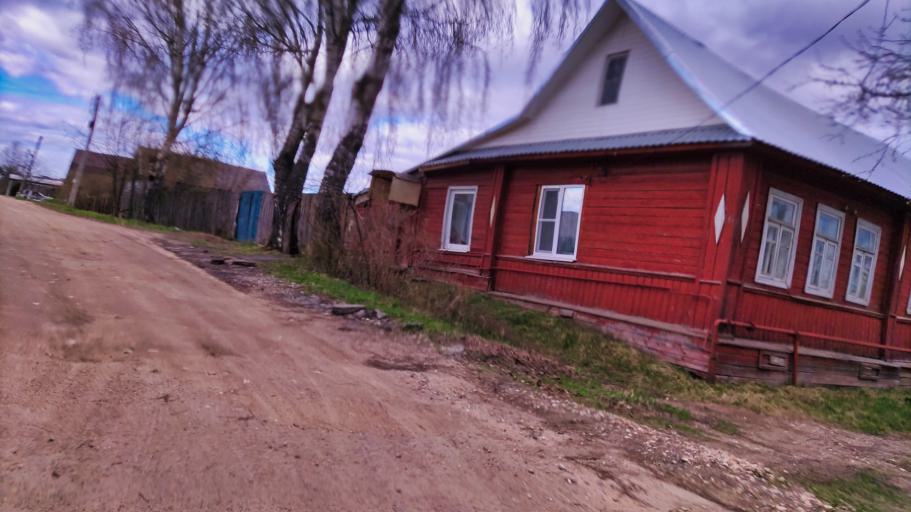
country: RU
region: Tverskaya
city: Rzhev
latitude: 56.2491
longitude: 34.3433
